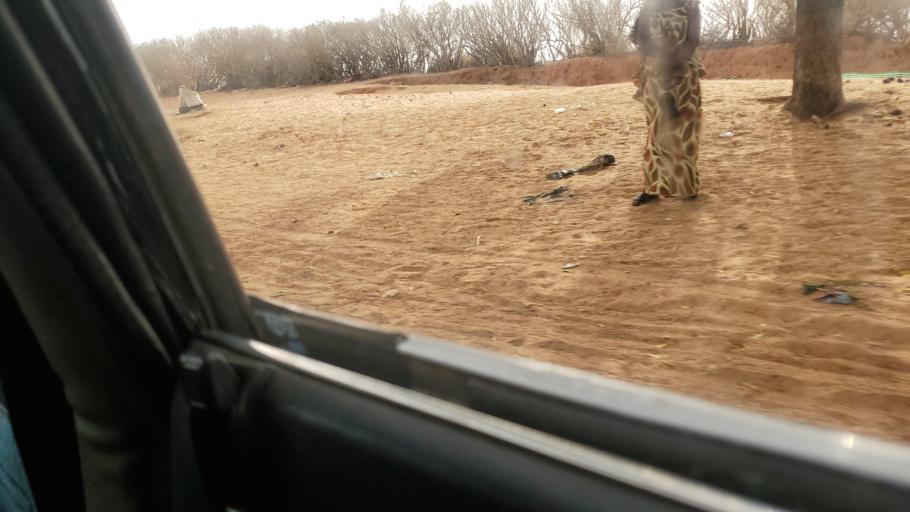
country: SN
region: Louga
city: Louga
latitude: 15.7795
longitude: -16.2537
